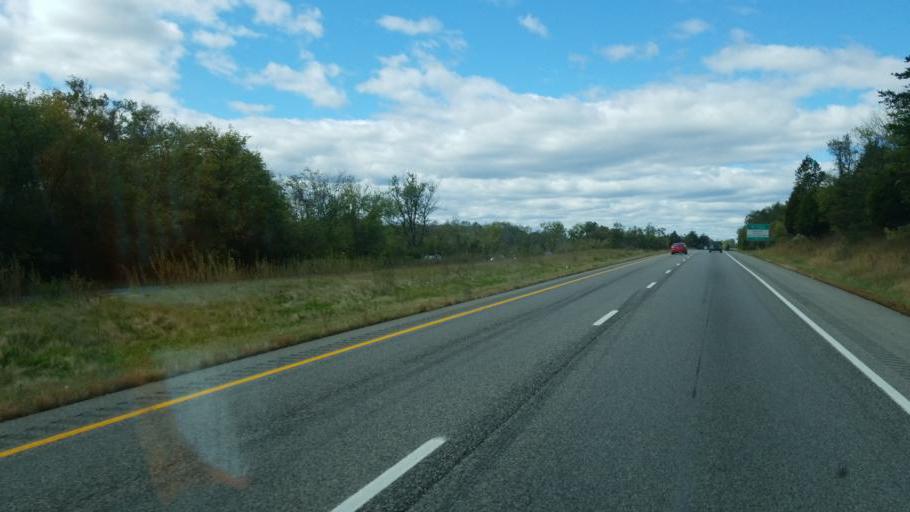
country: US
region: Maryland
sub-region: Washington County
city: Hancock
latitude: 39.6434
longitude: -78.0352
